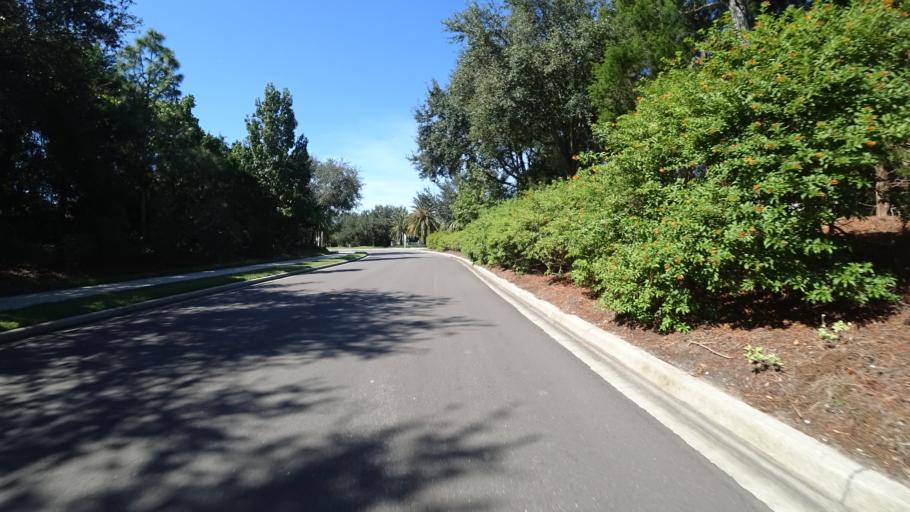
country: US
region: Florida
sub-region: Sarasota County
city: The Meadows
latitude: 27.4139
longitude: -82.4075
